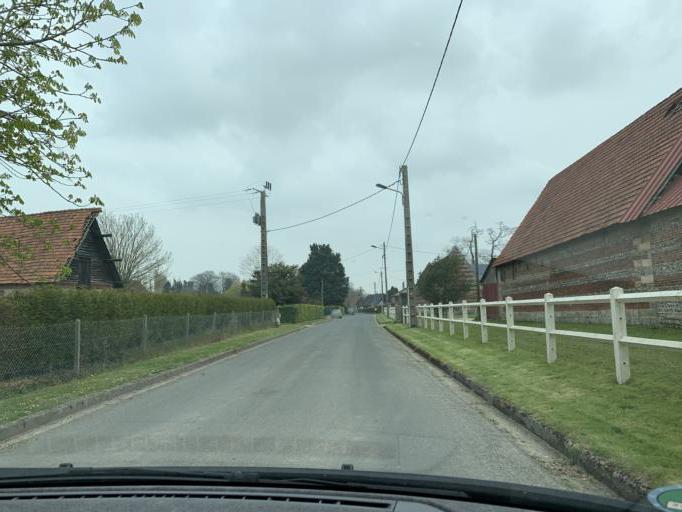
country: FR
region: Haute-Normandie
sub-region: Departement de la Seine-Maritime
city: Saint-Valery-en-Caux
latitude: 49.8544
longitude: 0.7965
